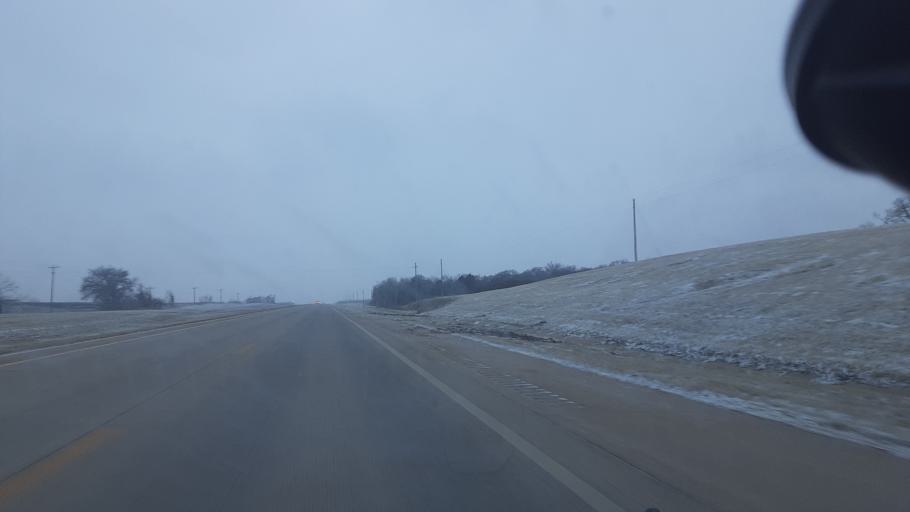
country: US
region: Oklahoma
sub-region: Payne County
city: Perkins
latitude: 35.9859
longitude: -97.1255
